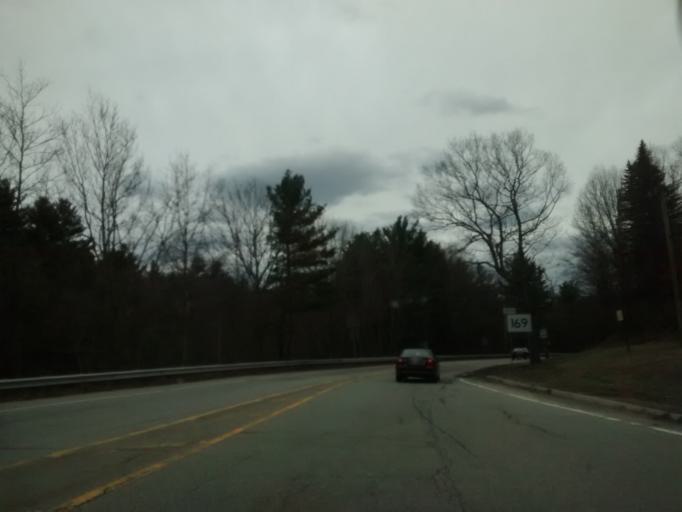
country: US
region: Massachusetts
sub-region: Worcester County
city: Charlton
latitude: 42.1443
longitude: -71.9947
